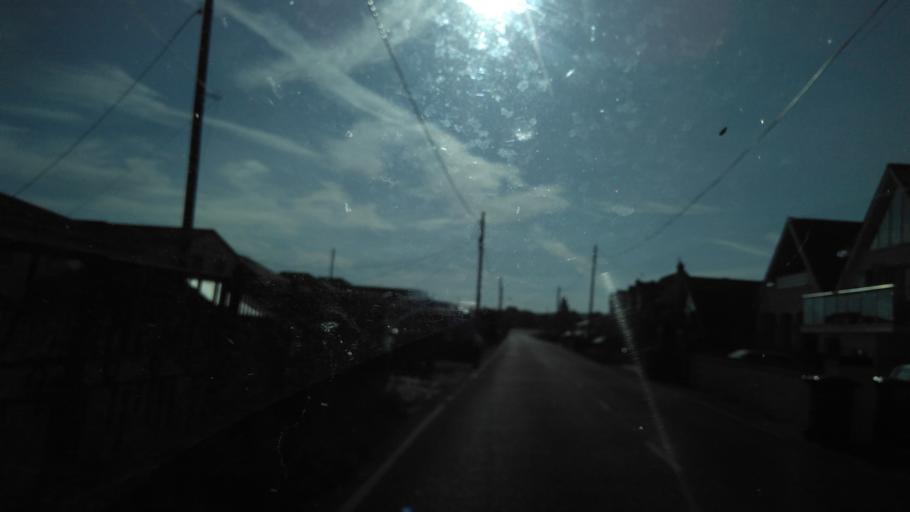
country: GB
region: England
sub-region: Kent
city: Whitstable
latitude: 51.3463
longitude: 0.9849
